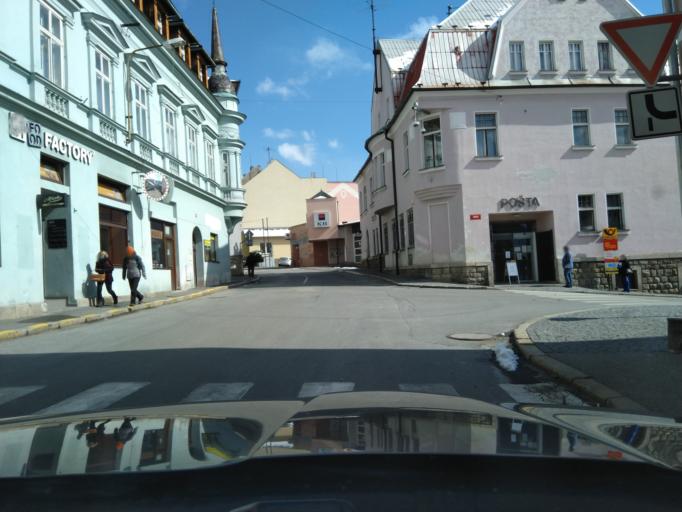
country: CZ
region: Jihocesky
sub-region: Okres Prachatice
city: Vimperk
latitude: 49.0536
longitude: 13.7767
